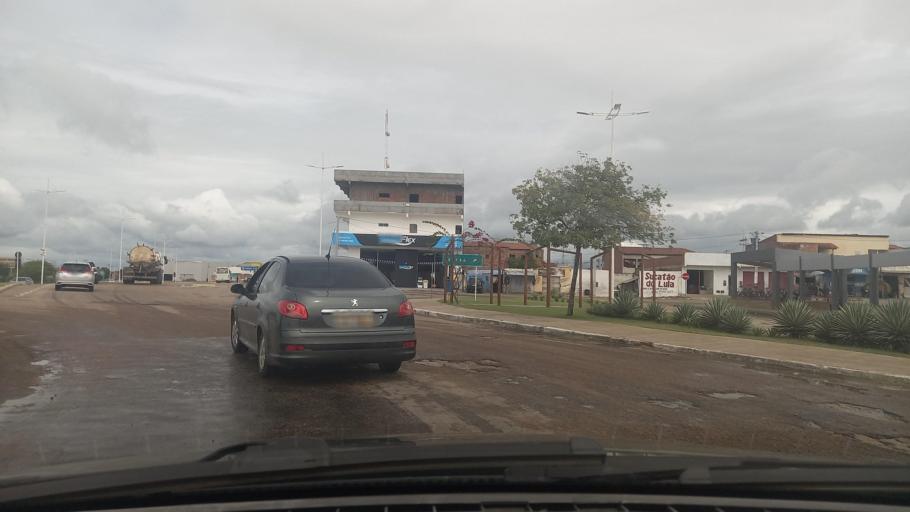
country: BR
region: Bahia
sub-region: Paulo Afonso
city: Paulo Afonso
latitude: -9.4467
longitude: -38.2220
